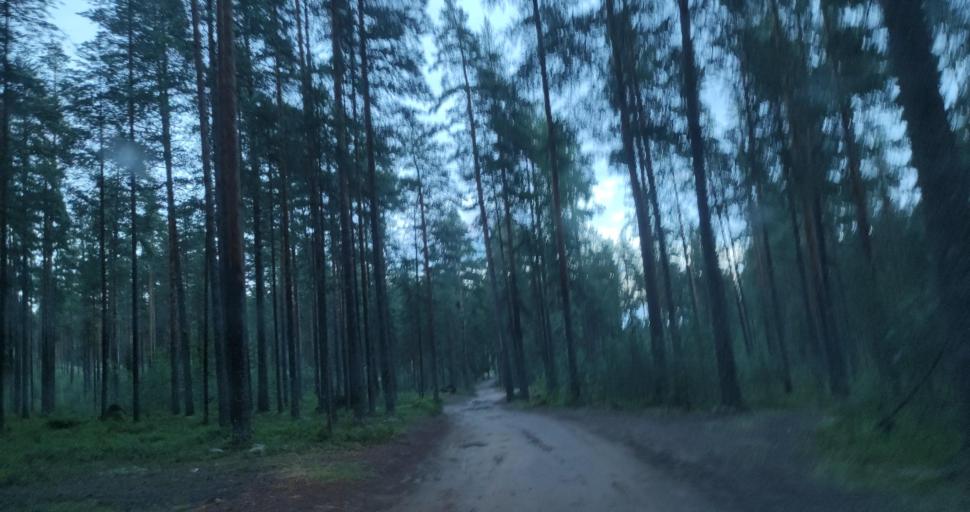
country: RU
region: Leningrad
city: Sapernoye
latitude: 60.6755
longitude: 29.9330
